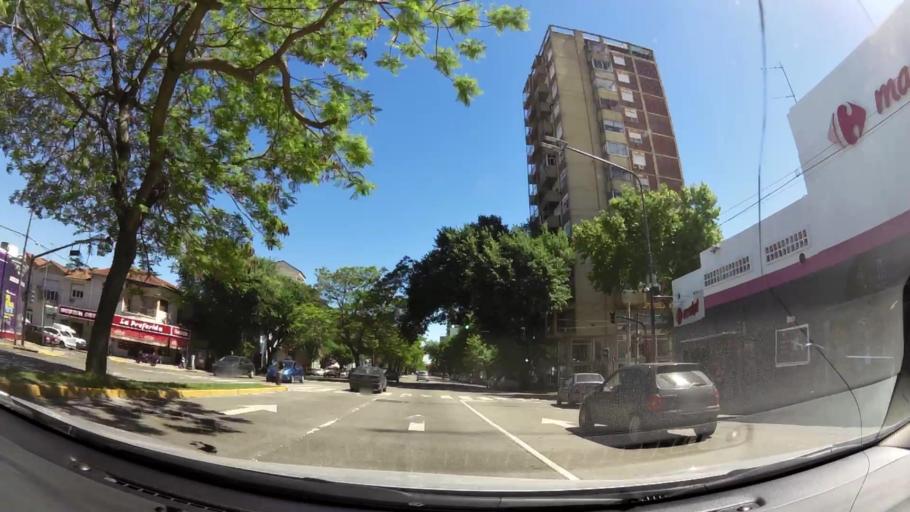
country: AR
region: Buenos Aires
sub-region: Partido de Vicente Lopez
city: Olivos
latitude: -34.5047
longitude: -58.4941
